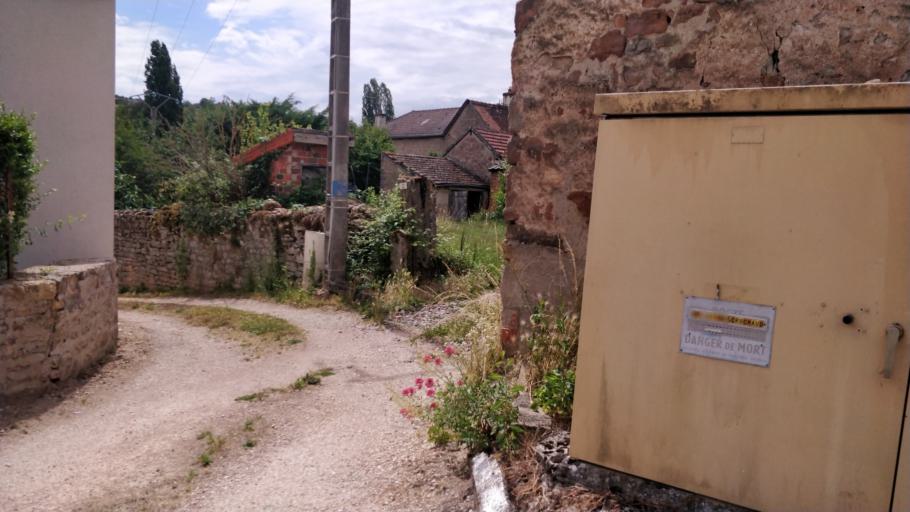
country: FR
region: Bourgogne
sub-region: Departement de Saone-et-Loire
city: Buxy
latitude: 46.7318
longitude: 4.6848
